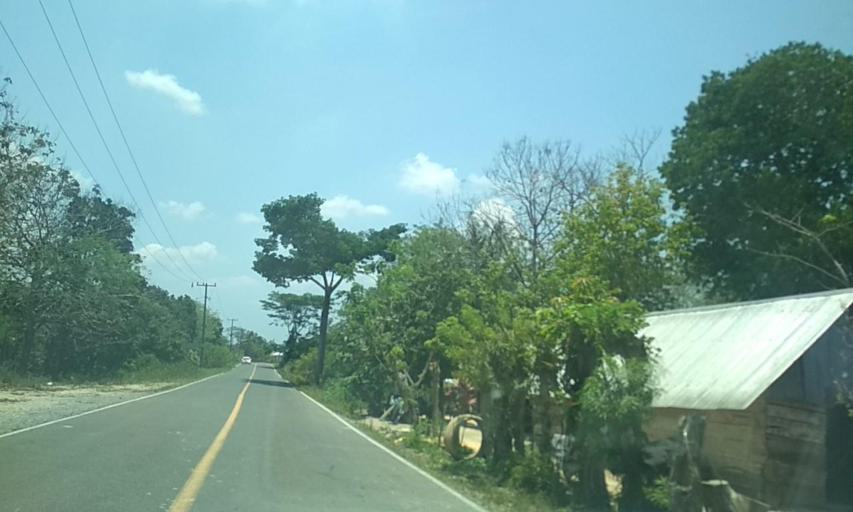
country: MX
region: Tabasco
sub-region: Huimanguillo
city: Francisco Rueda
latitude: 17.7651
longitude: -94.0593
